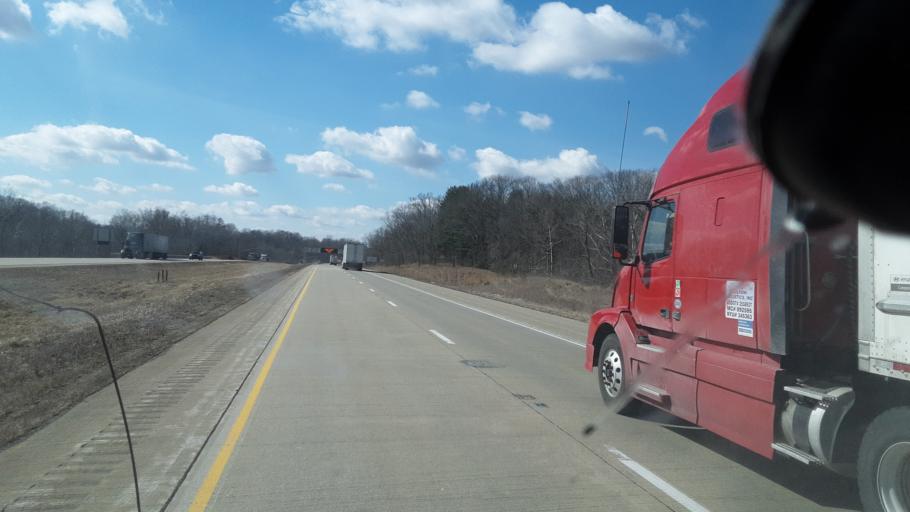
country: US
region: Indiana
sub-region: Vigo County
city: West Terre Haute
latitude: 39.4330
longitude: -87.5399
